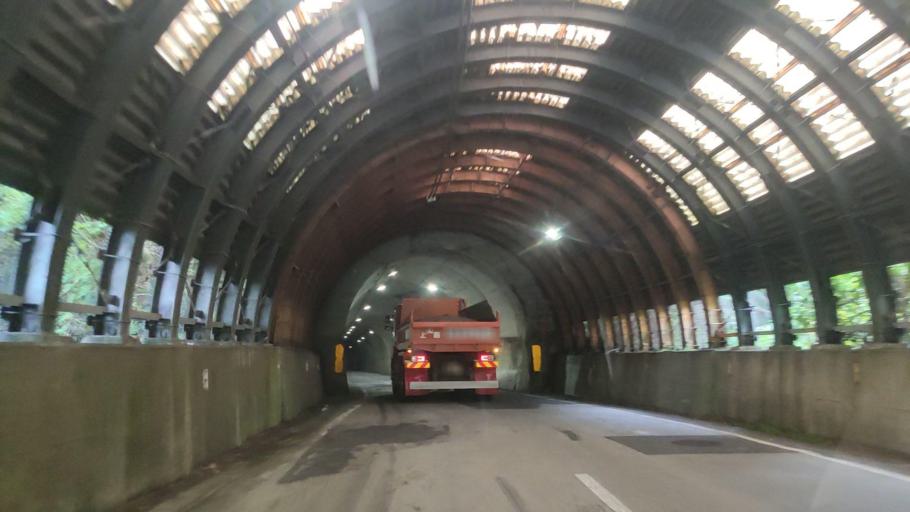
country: JP
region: Nagano
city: Iiyama
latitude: 36.8788
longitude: 138.3189
